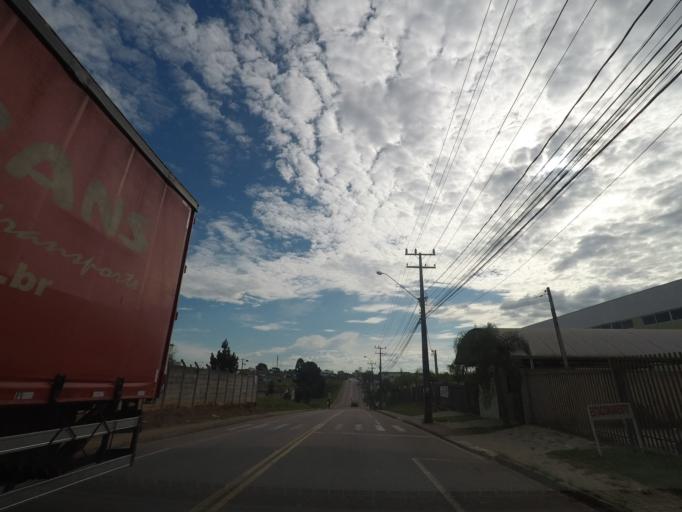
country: BR
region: Parana
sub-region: Araucaria
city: Araucaria
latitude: -25.6411
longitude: -49.3073
